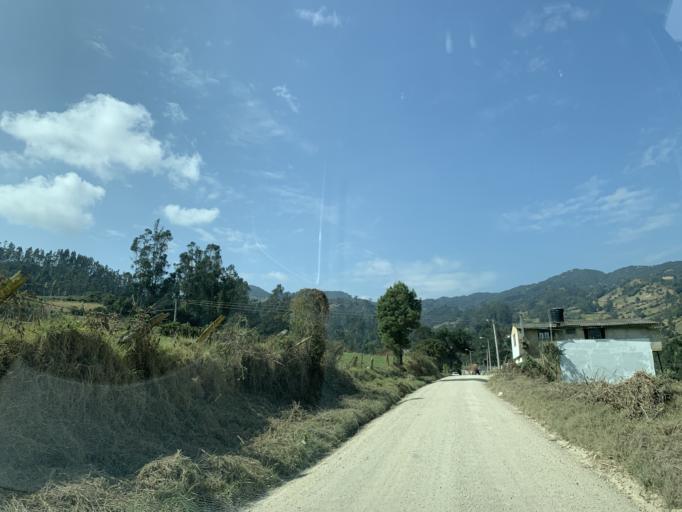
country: CO
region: Boyaca
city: Turmeque
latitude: 5.2835
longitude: -73.5038
